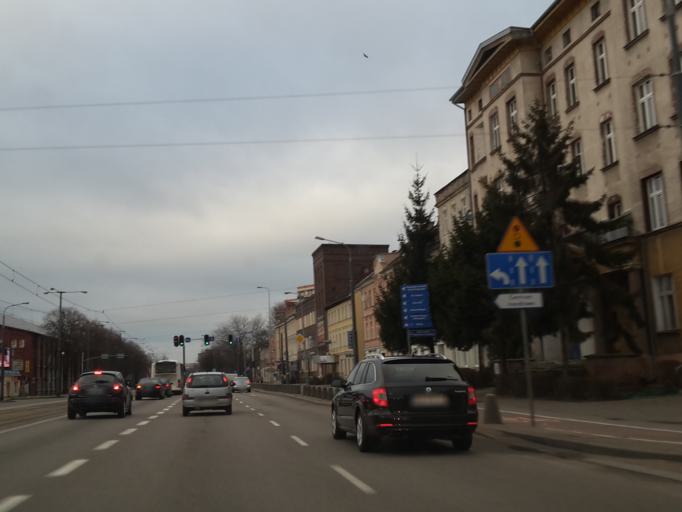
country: PL
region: Warmian-Masurian Voivodeship
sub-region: Powiat elblaski
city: Elblag
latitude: 54.1535
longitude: 19.4143
